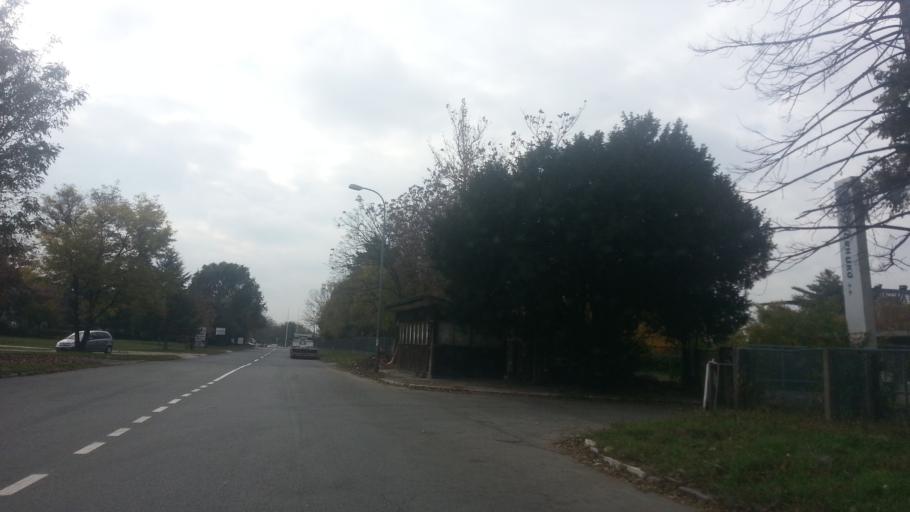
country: RS
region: Central Serbia
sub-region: Belgrade
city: Zemun
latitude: 44.8609
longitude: 20.3669
